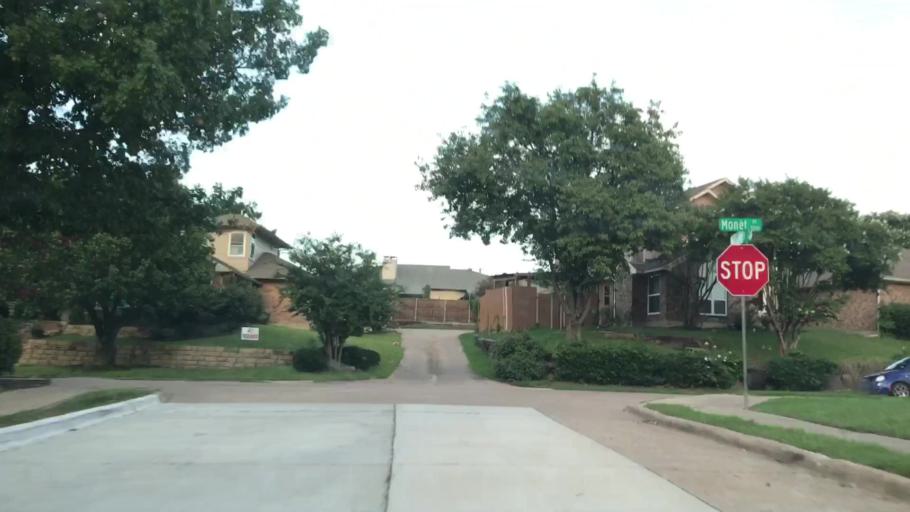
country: US
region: Texas
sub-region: Dallas County
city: Addison
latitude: 33.0055
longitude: -96.8617
